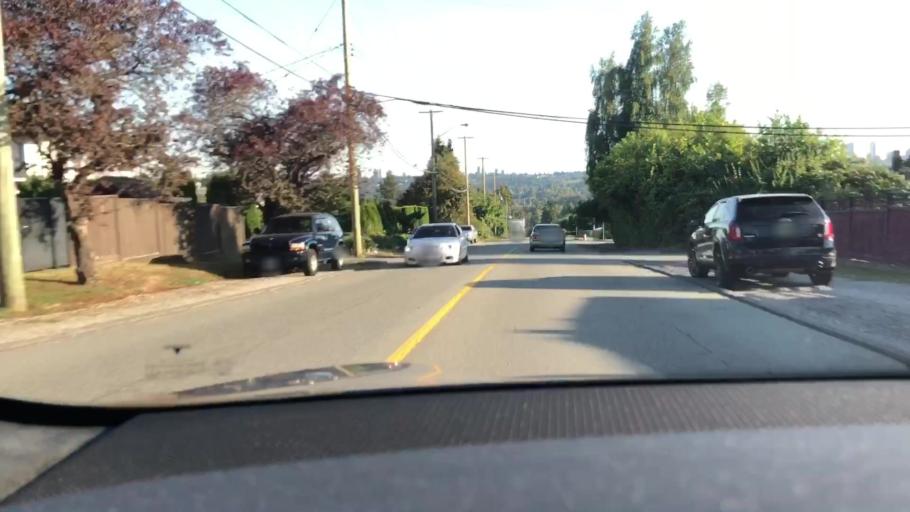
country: CA
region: British Columbia
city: Burnaby
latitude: 49.2678
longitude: -122.9701
